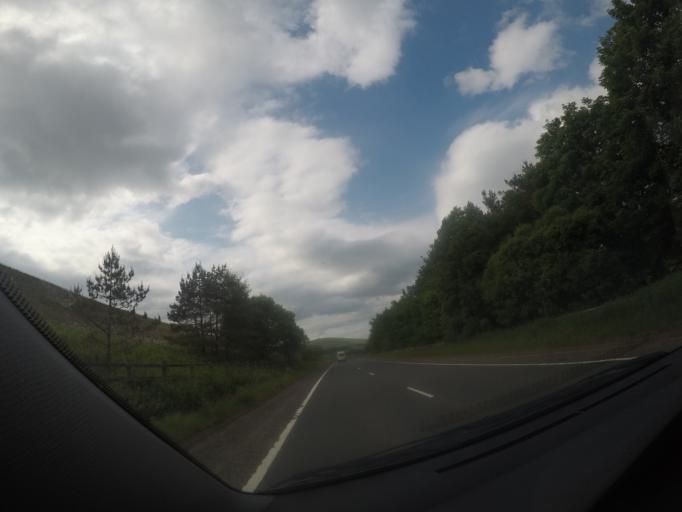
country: GB
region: Scotland
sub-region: South Lanarkshire
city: Douglas
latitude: 55.4747
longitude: -3.6945
